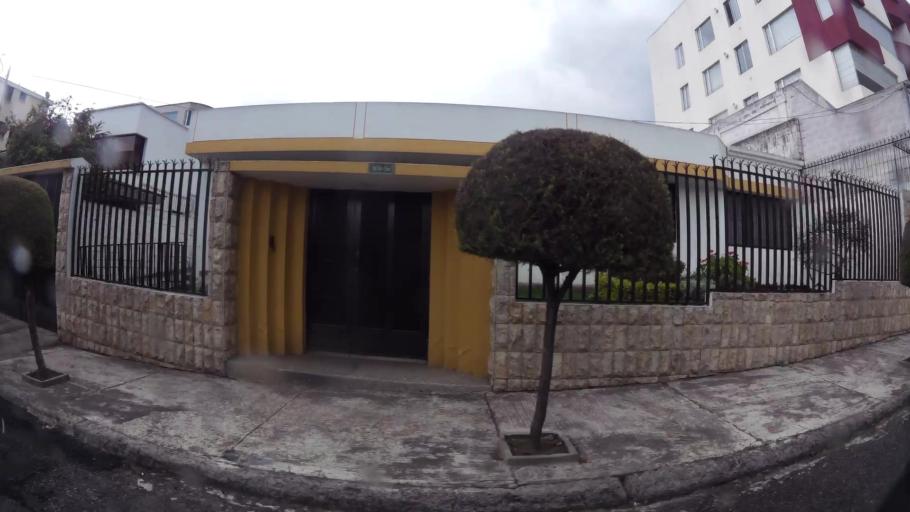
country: EC
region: Pichincha
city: Quito
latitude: -0.0996
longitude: -78.4810
